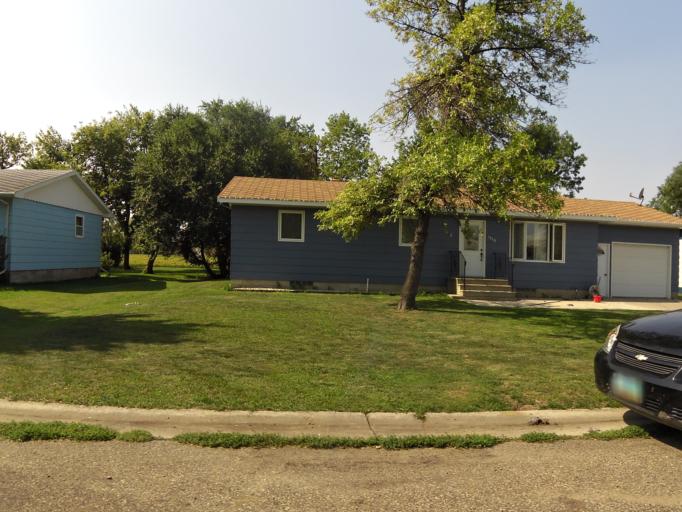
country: US
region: North Dakota
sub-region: Walsh County
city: Grafton
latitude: 48.4109
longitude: -97.3969
